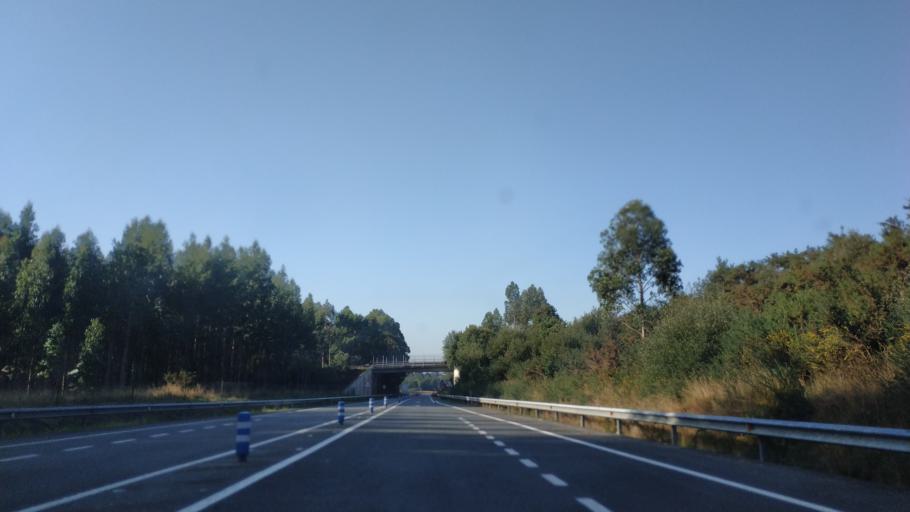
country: ES
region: Galicia
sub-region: Provincia da Coruna
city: Carballo
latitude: 43.2427
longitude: -8.6758
